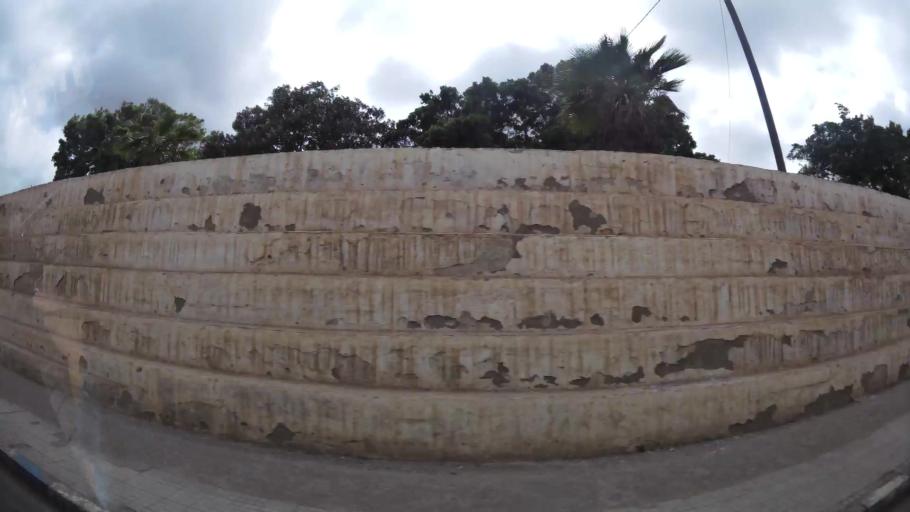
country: MA
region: Oriental
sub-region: Nador
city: Nador
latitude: 35.1866
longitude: -2.9285
